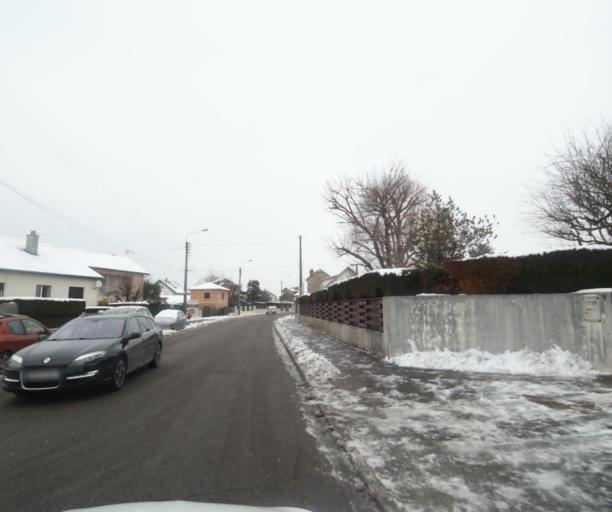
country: FR
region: Champagne-Ardenne
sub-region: Departement de la Haute-Marne
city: Saint-Dizier
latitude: 48.6333
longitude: 4.9361
